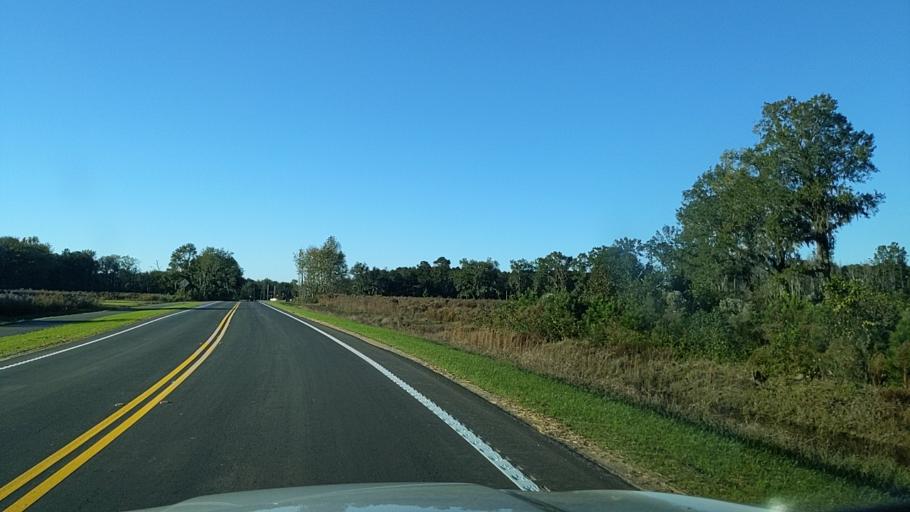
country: US
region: Georgia
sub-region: Chatham County
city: Port Wentworth
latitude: 32.1893
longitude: -81.2208
